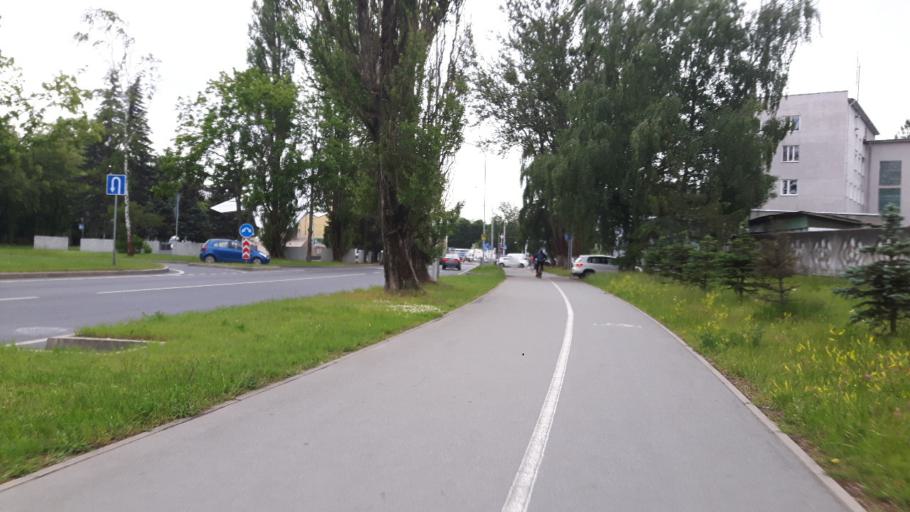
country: RU
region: Kaliningrad
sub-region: Gorod Kaliningrad
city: Kaliningrad
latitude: 54.7320
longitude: 20.4904
